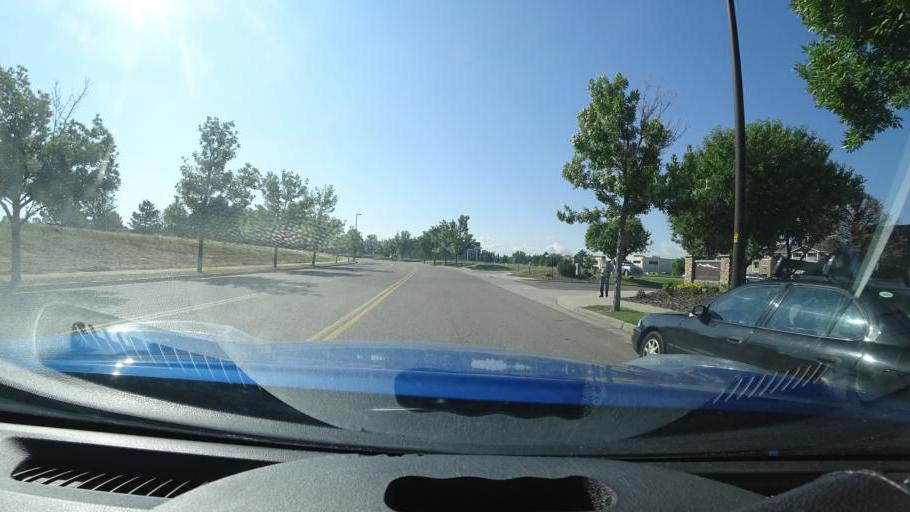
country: US
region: Colorado
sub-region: Adams County
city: Aurora
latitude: 39.7218
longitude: -104.8060
